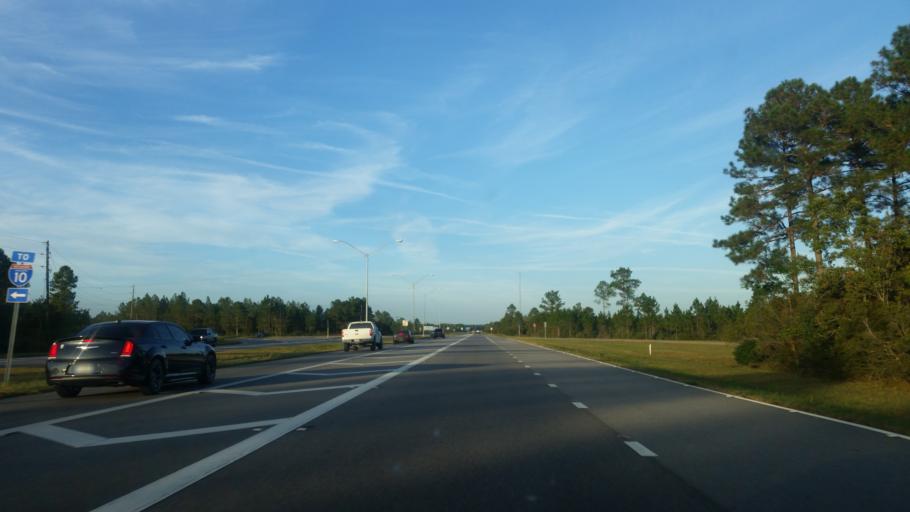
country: US
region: Alabama
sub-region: Mobile County
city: Grand Bay
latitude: 30.4563
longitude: -88.4188
